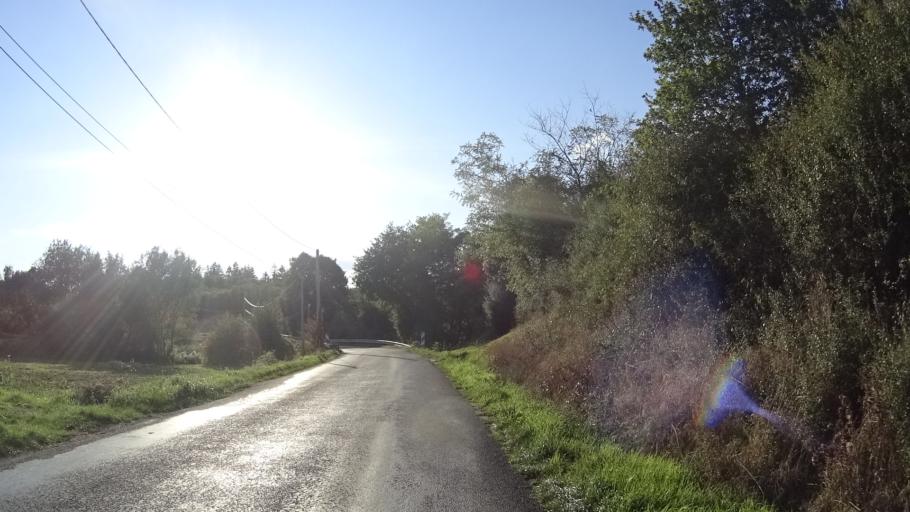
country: FR
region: Pays de la Loire
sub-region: Departement de Maine-et-Loire
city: Bouzille
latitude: 47.3441
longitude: -1.0845
